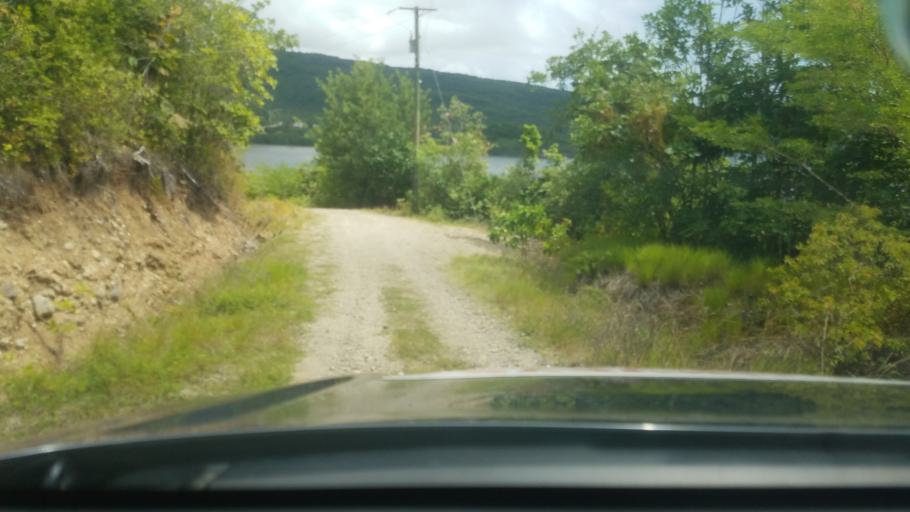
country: LC
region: Praslin
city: Praslin
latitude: 13.8679
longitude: -60.8942
